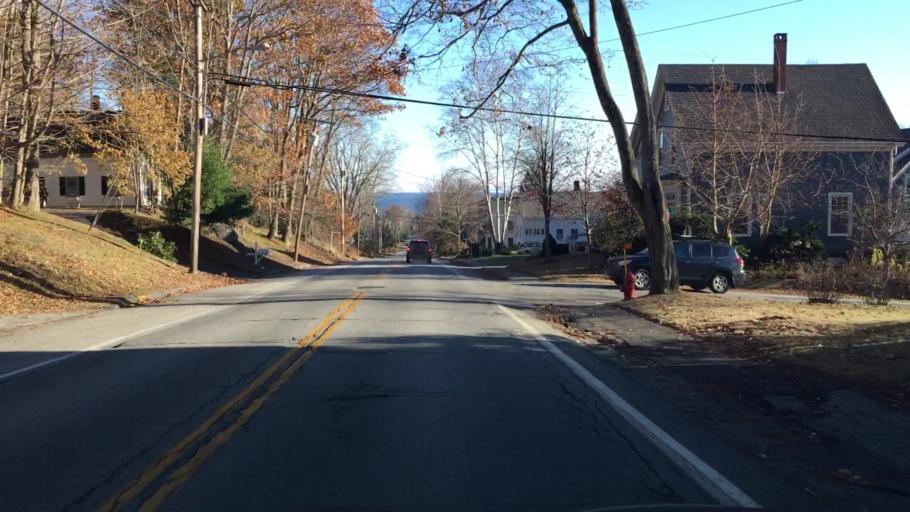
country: US
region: Maine
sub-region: Knox County
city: Camden
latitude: 44.2161
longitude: -69.0713
